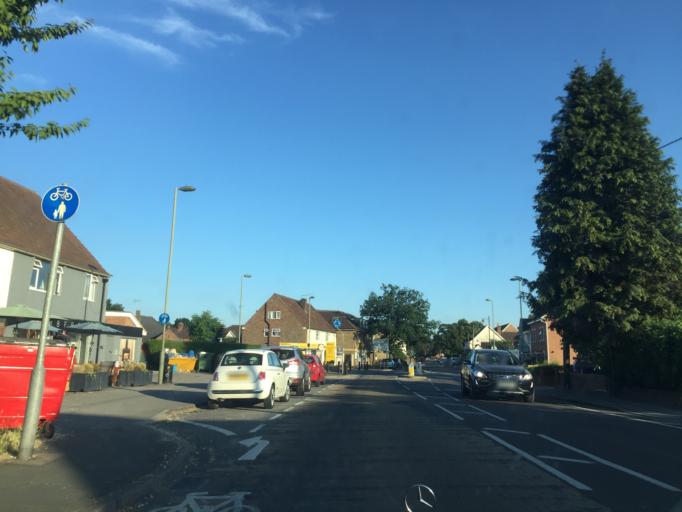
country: GB
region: England
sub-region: Surrey
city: Frimley
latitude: 51.3049
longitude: -0.7293
